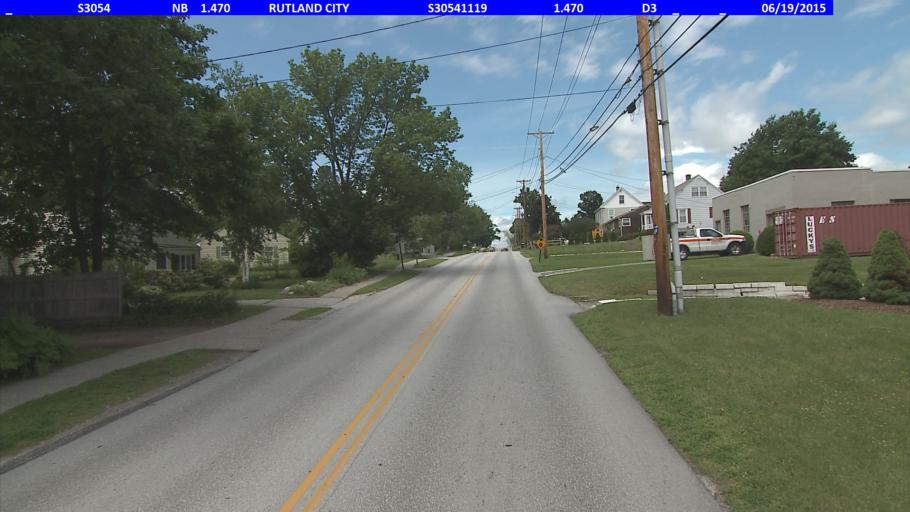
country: US
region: Vermont
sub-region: Rutland County
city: Rutland
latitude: 43.6124
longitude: -72.9566
